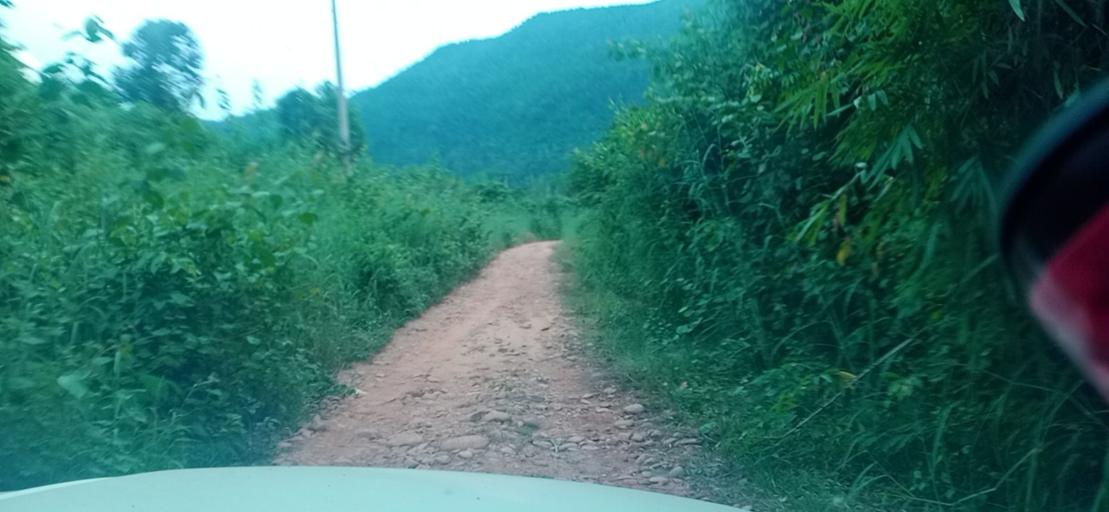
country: TH
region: Changwat Bueng Kan
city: Pak Khat
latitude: 18.5617
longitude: 103.2910
